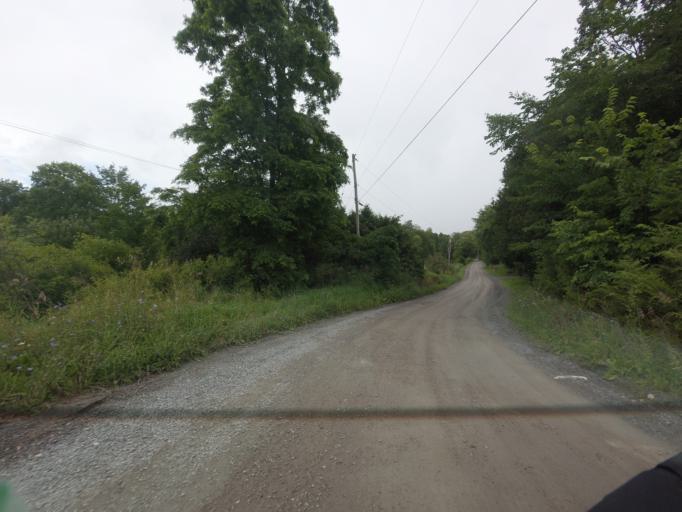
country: CA
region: Ontario
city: Kingston
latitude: 44.5913
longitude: -76.5303
